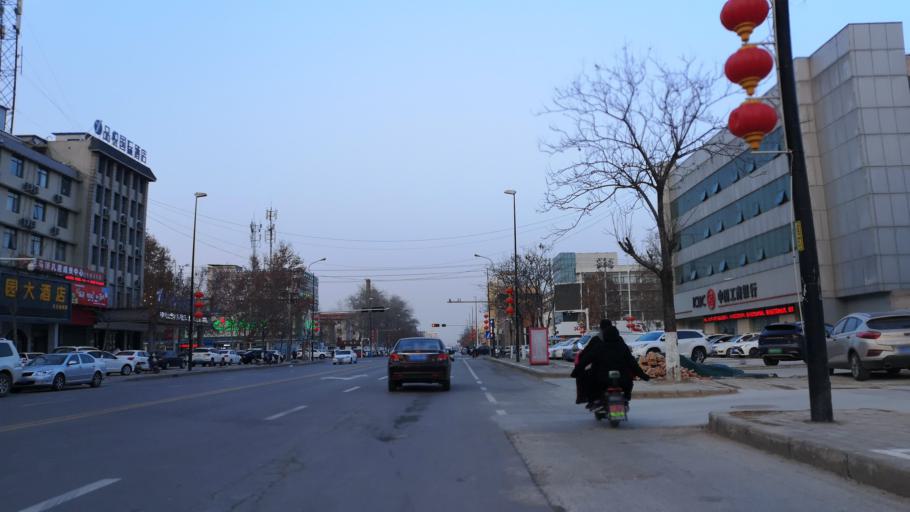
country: CN
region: Henan Sheng
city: Zhongyuanlu
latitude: 35.7772
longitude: 115.0604
